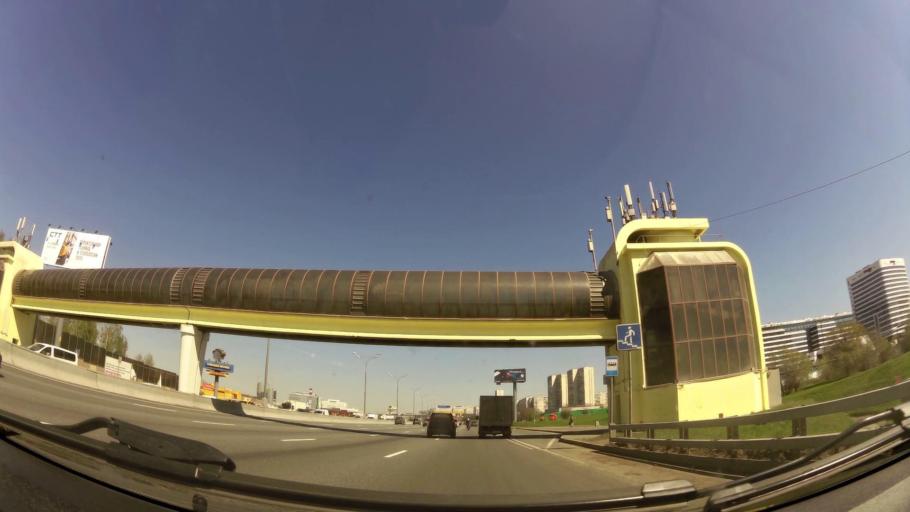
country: RU
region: Moscow
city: Strogino
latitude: 55.8026
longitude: 37.3850
